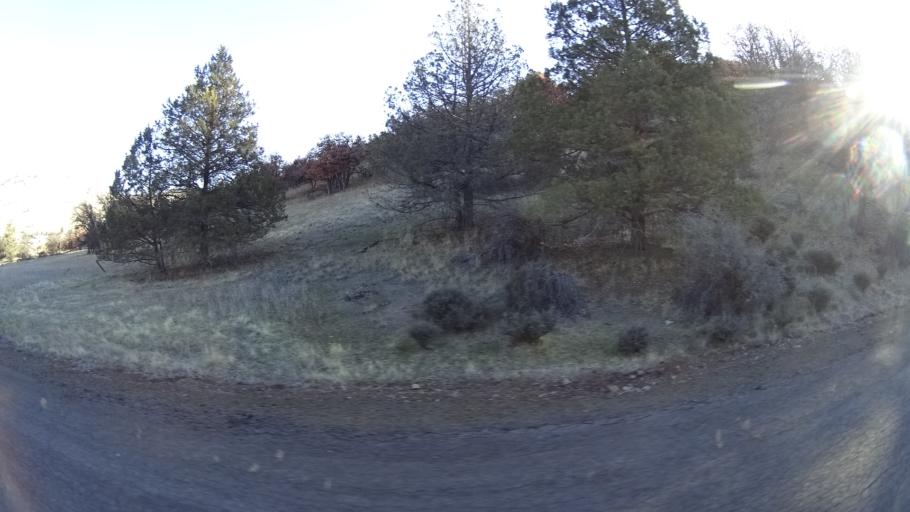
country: US
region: California
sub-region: Siskiyou County
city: Montague
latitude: 41.8943
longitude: -122.5004
